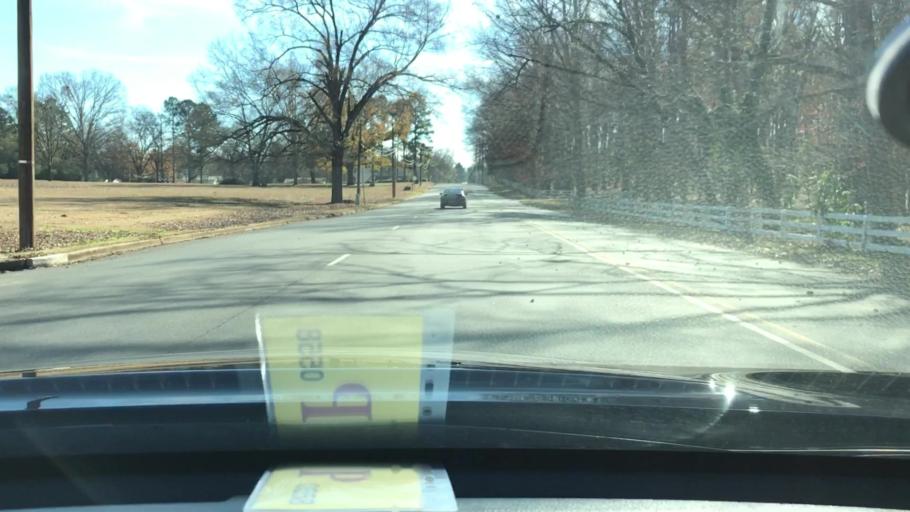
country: US
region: Alabama
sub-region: Talladega County
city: Mignon
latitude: 33.1805
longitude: -86.2637
